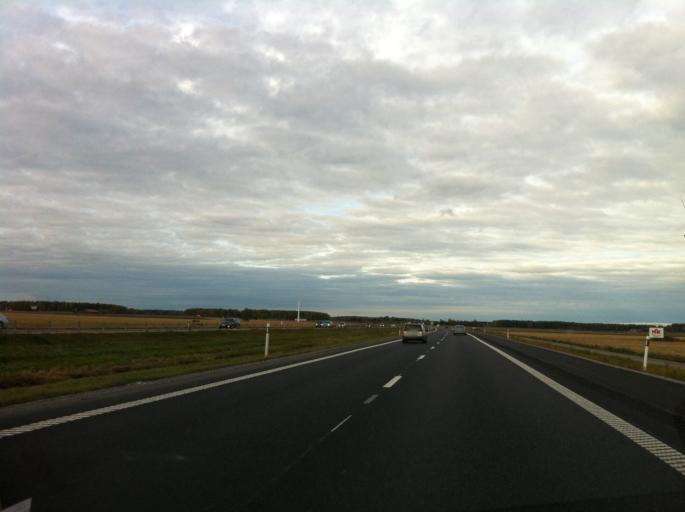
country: SE
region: OErebro
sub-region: Kumla Kommun
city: Kumla
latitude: 59.1652
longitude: 15.1104
